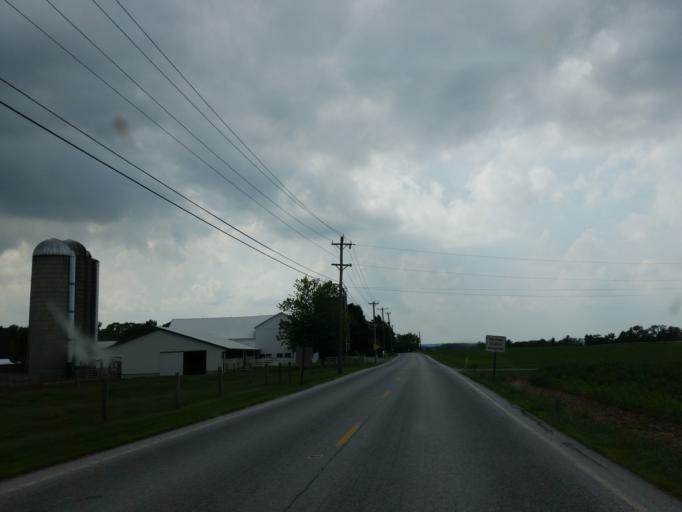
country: US
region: Pennsylvania
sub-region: Chester County
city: Oxford
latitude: 39.8545
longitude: -75.9682
